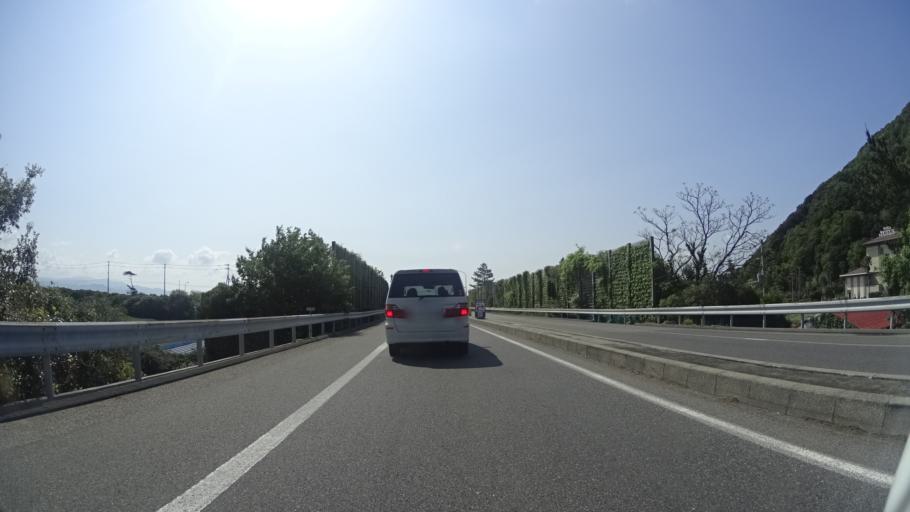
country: JP
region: Tokushima
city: Narutocho-mitsuishi
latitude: 34.2180
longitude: 134.6292
